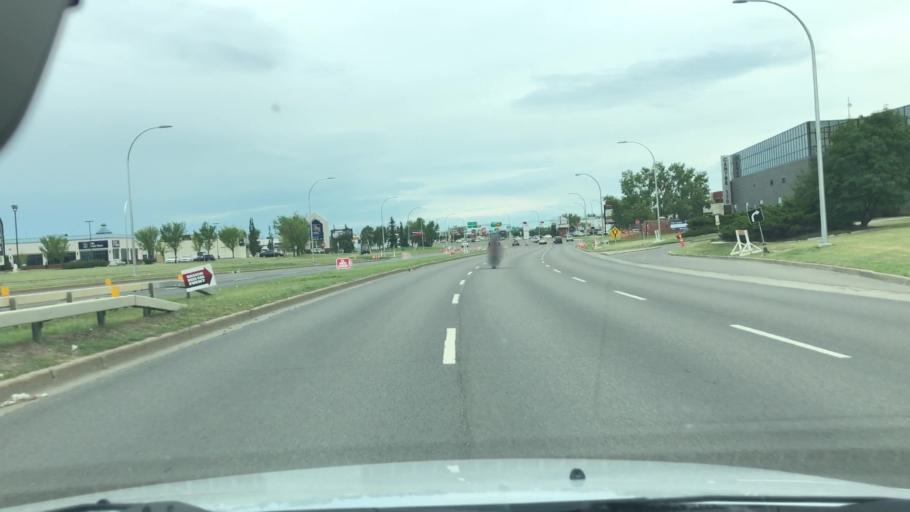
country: CA
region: Alberta
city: St. Albert
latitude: 53.5475
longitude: -113.6154
